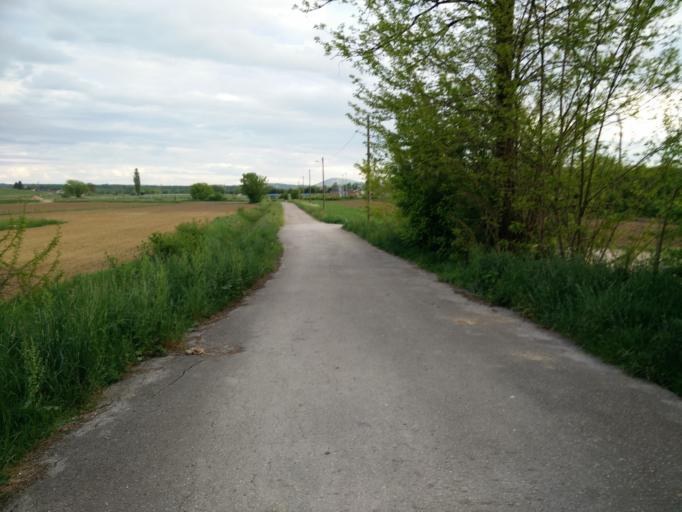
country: HR
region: Karlovacka
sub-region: Grad Karlovac
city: Karlovac
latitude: 45.4886
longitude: 15.5650
